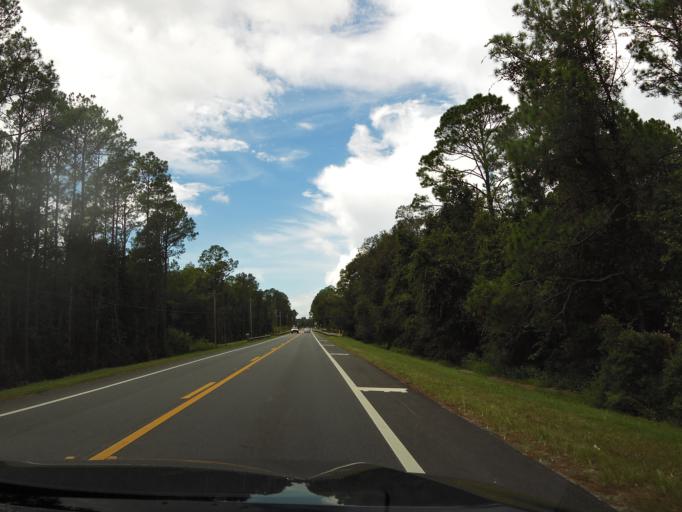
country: US
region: Florida
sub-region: Clay County
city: Middleburg
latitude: 30.1132
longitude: -81.9813
